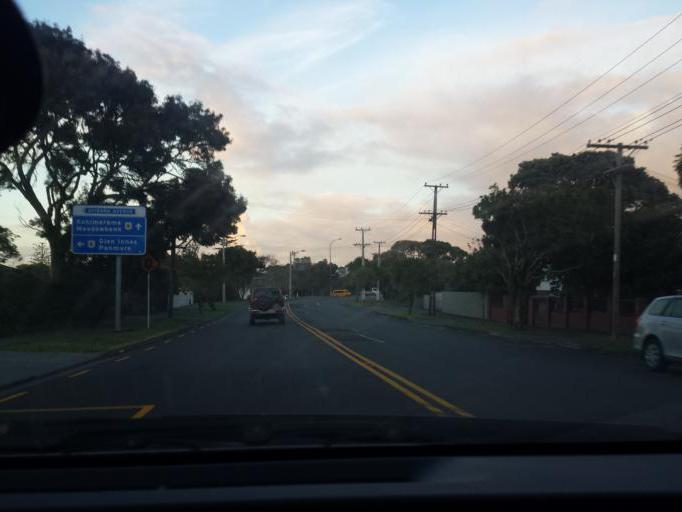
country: NZ
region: Auckland
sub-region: Auckland
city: Tamaki
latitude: -36.8673
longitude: 174.8498
